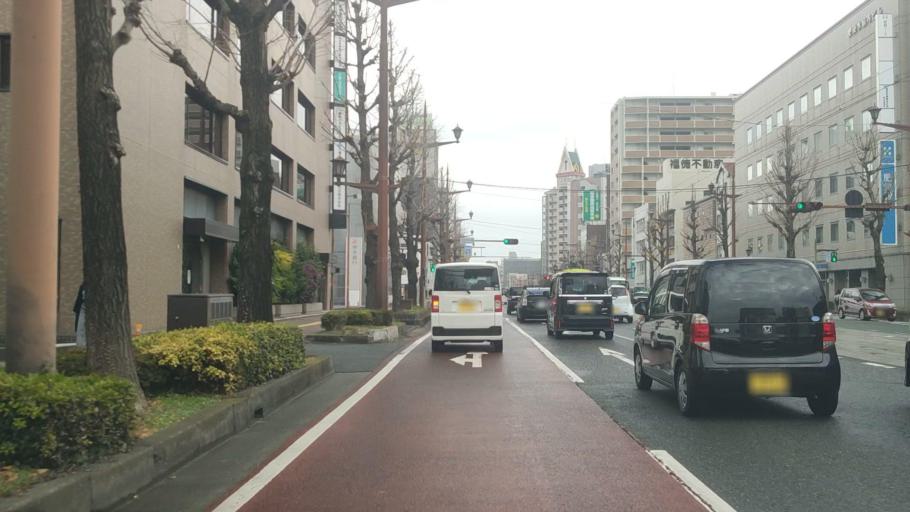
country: JP
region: Kumamoto
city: Kumamoto
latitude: 32.7924
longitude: 130.7287
